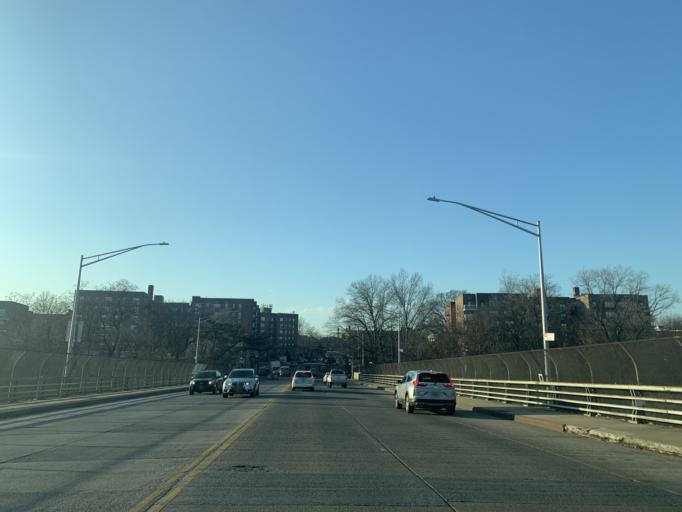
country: US
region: New York
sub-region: Westchester County
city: Mount Vernon
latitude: 40.9007
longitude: -73.8601
